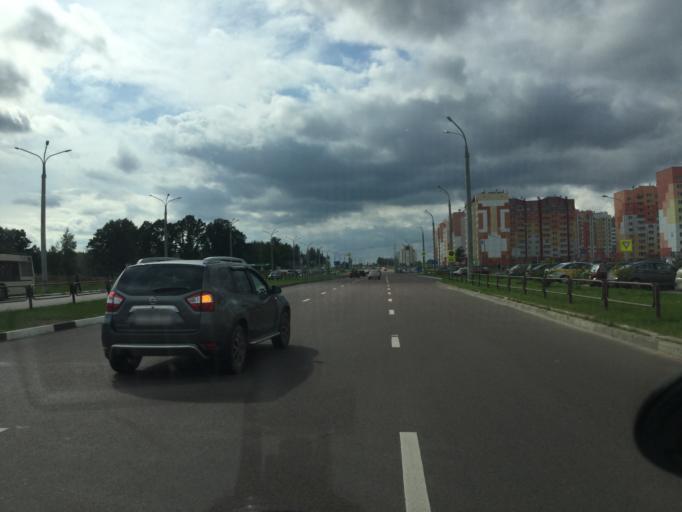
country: BY
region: Vitebsk
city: Vitebsk
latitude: 55.1660
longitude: 30.2886
